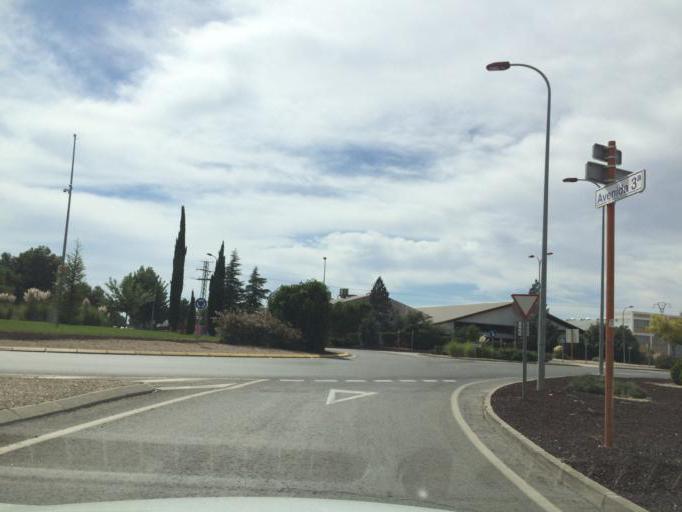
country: ES
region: Castille-La Mancha
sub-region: Provincia de Albacete
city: Albacete
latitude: 39.0149
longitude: -1.8783
